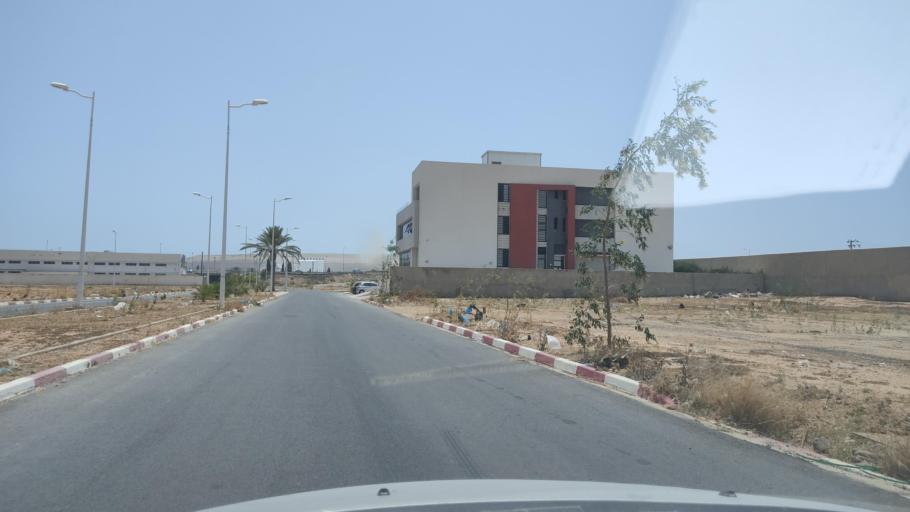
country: TN
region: Safaqis
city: Sfax
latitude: 34.7089
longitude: 10.7198
